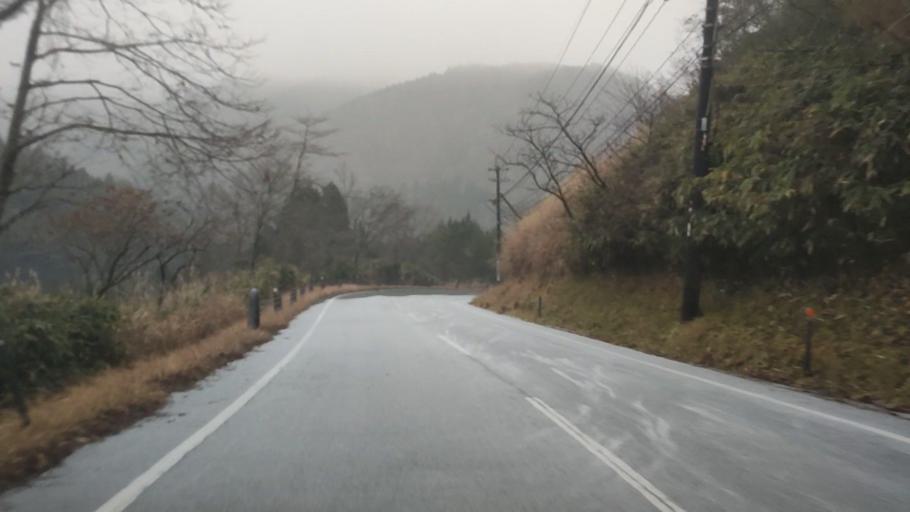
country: JP
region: Kumamoto
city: Matsubase
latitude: 32.5698
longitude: 130.9087
